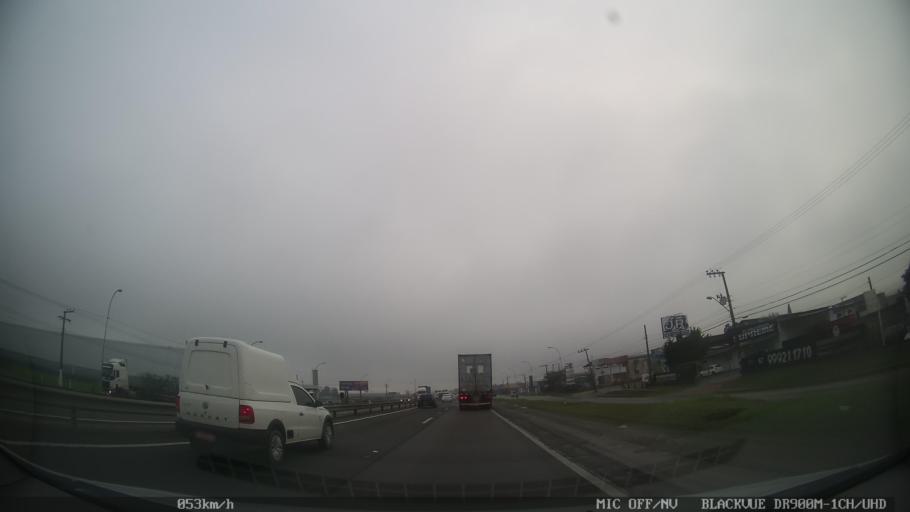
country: BR
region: Santa Catarina
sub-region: Itajai
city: Itajai
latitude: -26.8632
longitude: -48.7287
